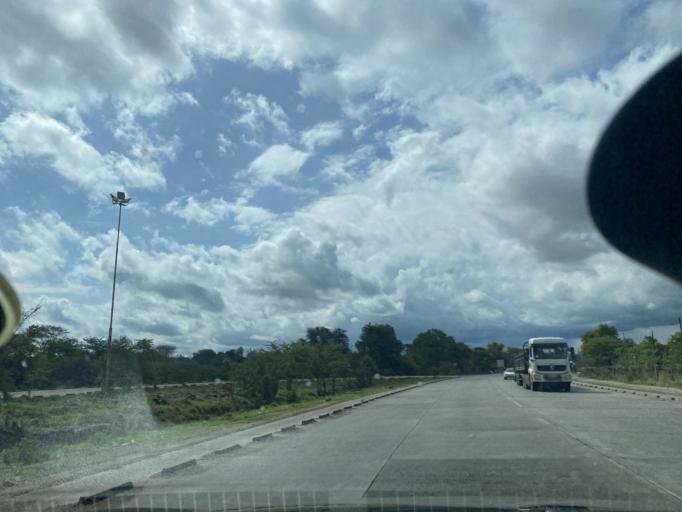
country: ZM
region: Lusaka
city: Kafue
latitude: -15.8449
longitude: 28.2424
